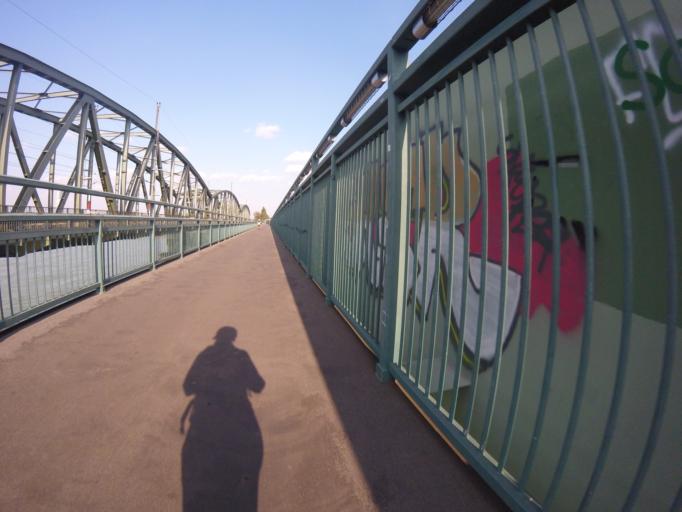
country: NE
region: Dosso
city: Dosso
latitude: 12.7082
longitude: 3.0521
